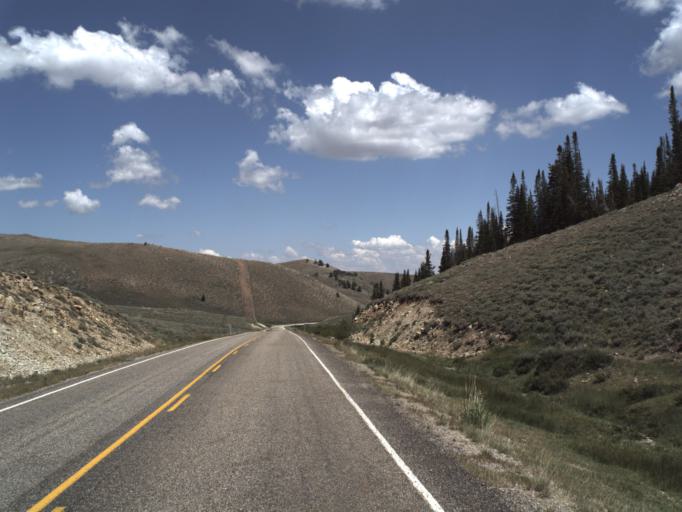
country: US
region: Utah
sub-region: Rich County
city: Randolph
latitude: 41.4832
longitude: -111.4190
